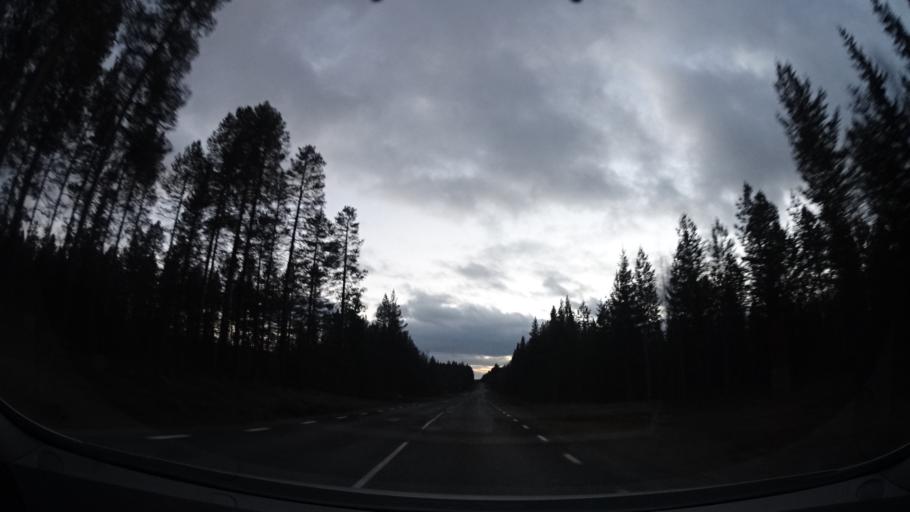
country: SE
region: Vaesterbotten
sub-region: Asele Kommun
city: Insjon
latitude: 64.2254
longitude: 17.5405
